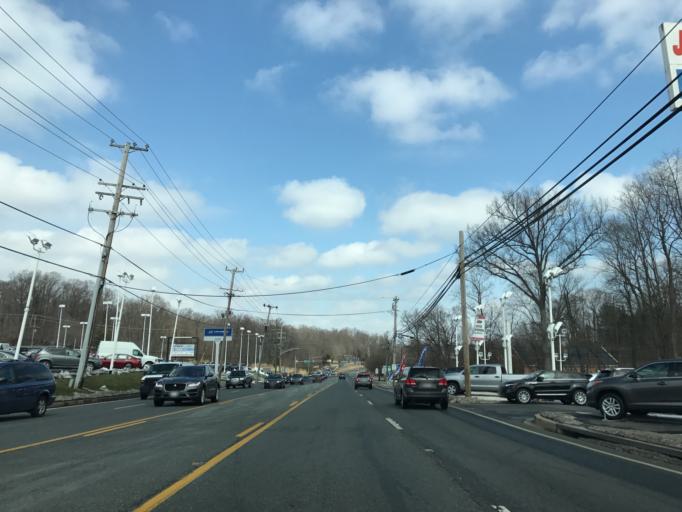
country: US
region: Maryland
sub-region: Harford County
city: Pleasant Hills
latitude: 39.5057
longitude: -76.3817
